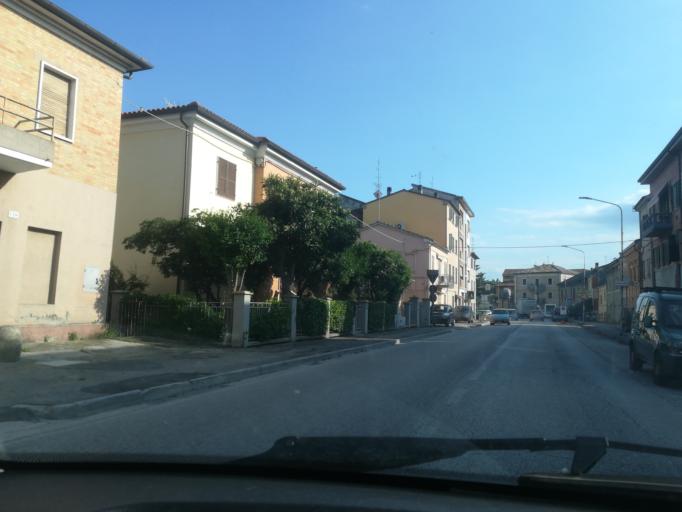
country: IT
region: The Marches
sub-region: Provincia di Macerata
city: Villa Potenza
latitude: 43.3250
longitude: 13.4264
